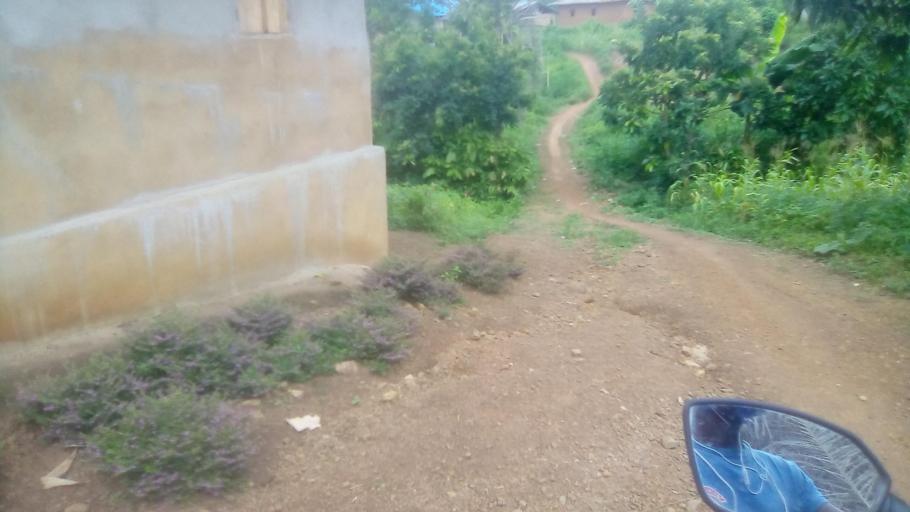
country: SL
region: Eastern Province
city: Kailahun
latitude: 8.2688
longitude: -10.5600
